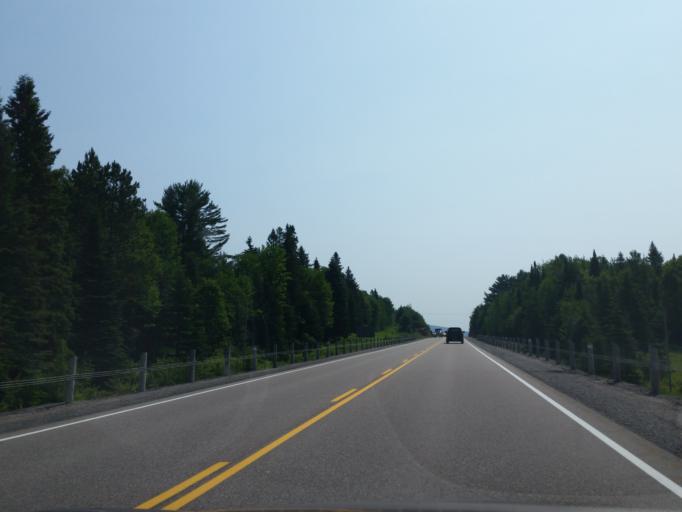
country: CA
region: Ontario
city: Mattawa
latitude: 46.3057
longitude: -78.6106
